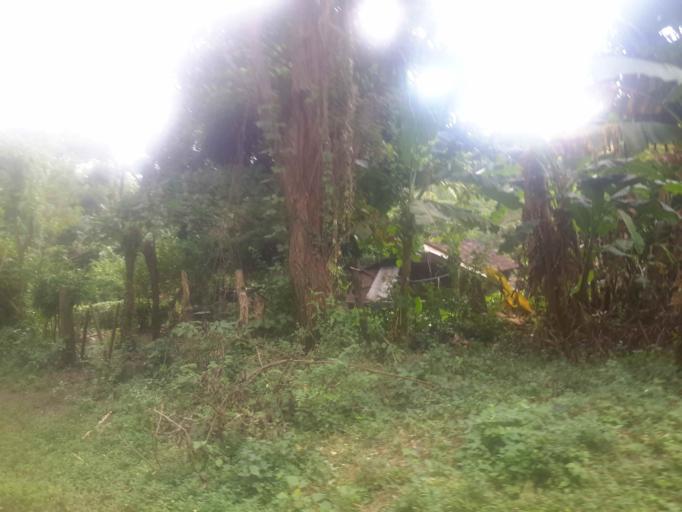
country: NI
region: Rivas
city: Altagracia
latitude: 11.5105
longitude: -85.6052
